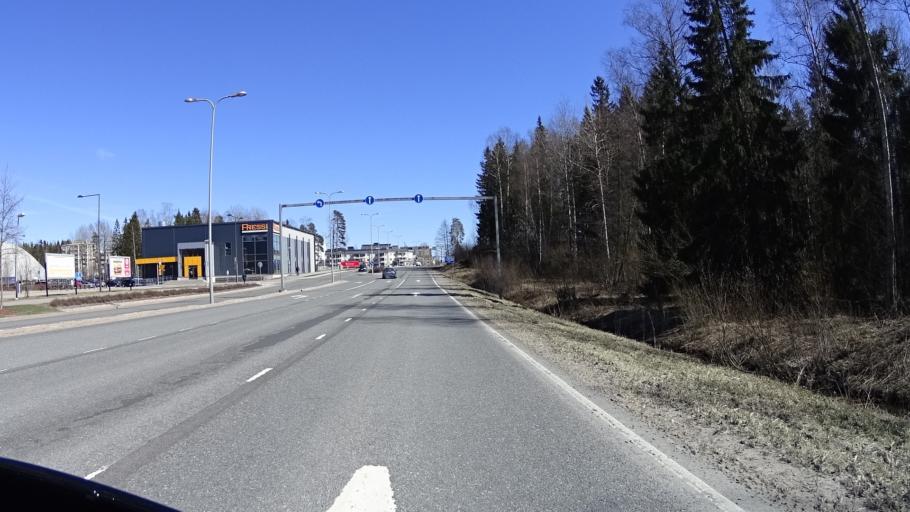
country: FI
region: Uusimaa
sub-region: Helsinki
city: Teekkarikylae
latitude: 60.2592
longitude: 24.8388
